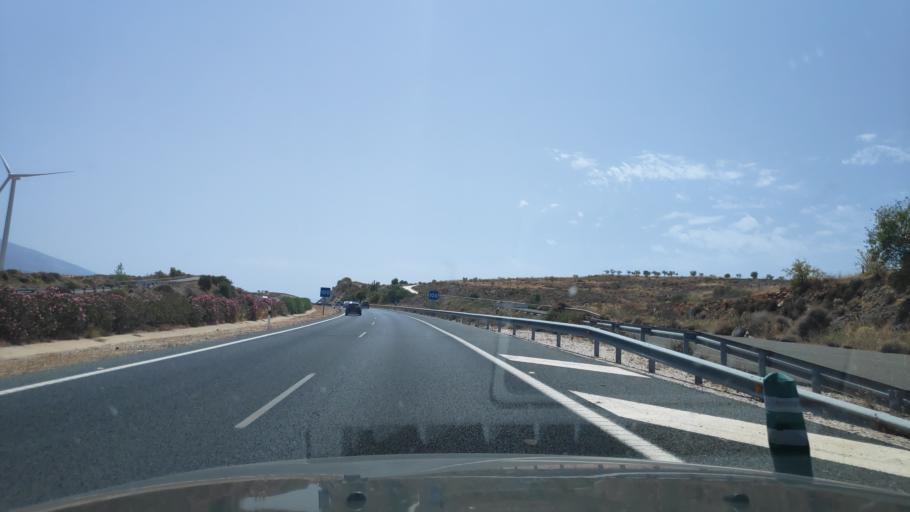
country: ES
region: Andalusia
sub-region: Provincia de Granada
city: Padul
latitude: 37.0058
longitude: -3.6379
